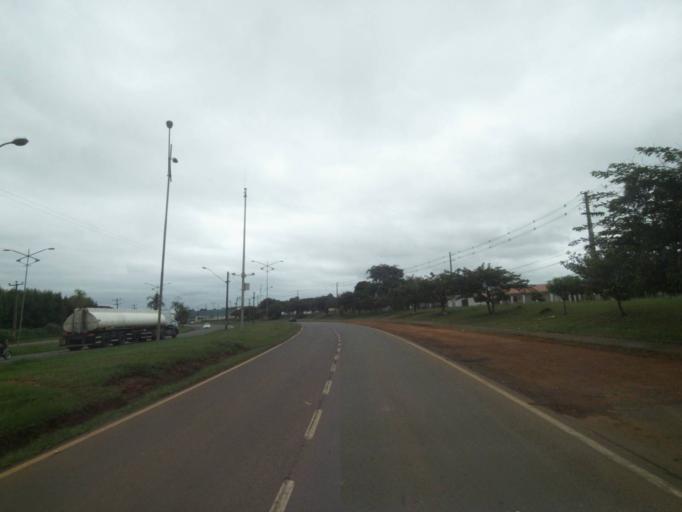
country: BR
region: Parana
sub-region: Telemaco Borba
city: Telemaco Borba
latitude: -24.3341
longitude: -50.6546
